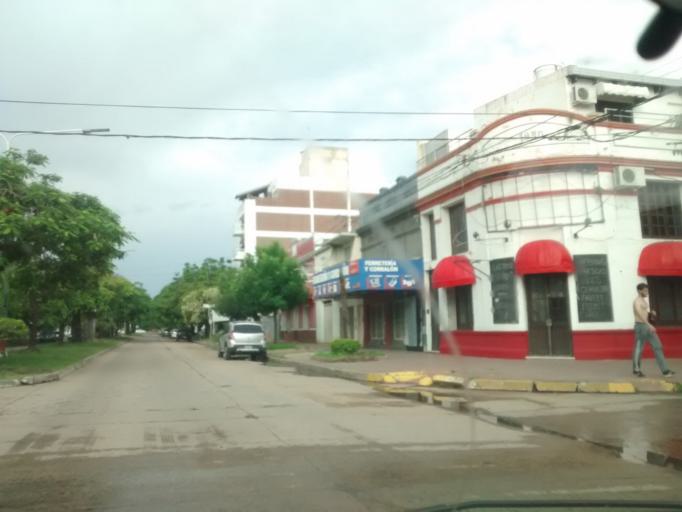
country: AR
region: Chaco
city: Resistencia
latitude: -27.4528
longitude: -58.9970
